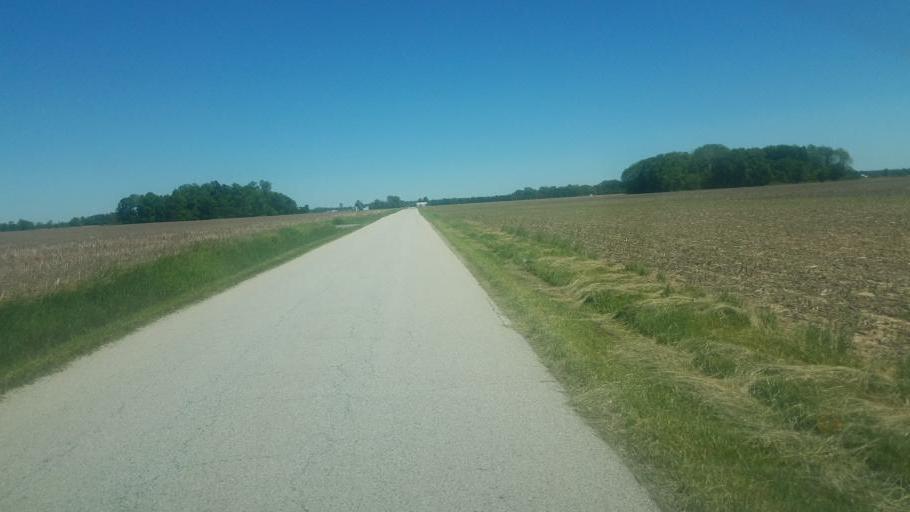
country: US
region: Ohio
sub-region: Shelby County
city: Sidney
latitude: 40.2006
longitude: -84.0750
